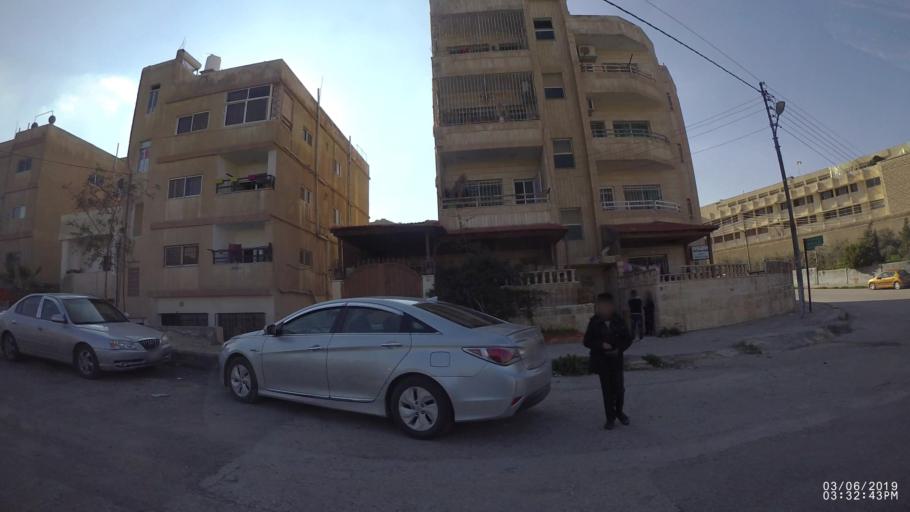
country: JO
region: Amman
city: Amman
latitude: 31.9757
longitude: 35.9648
